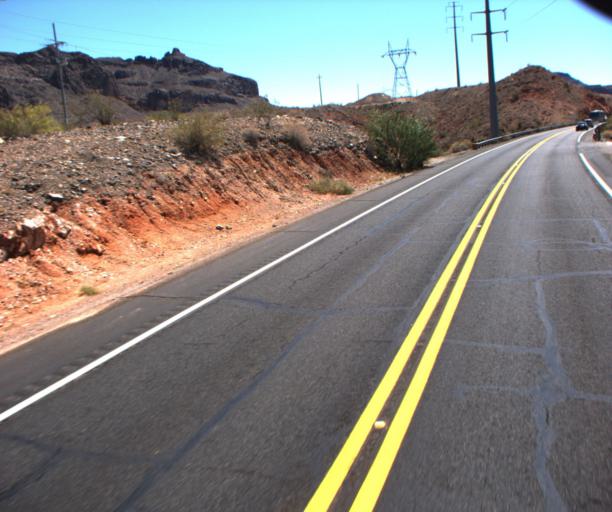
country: US
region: Arizona
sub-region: La Paz County
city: Cienega Springs
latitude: 34.2790
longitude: -114.1307
